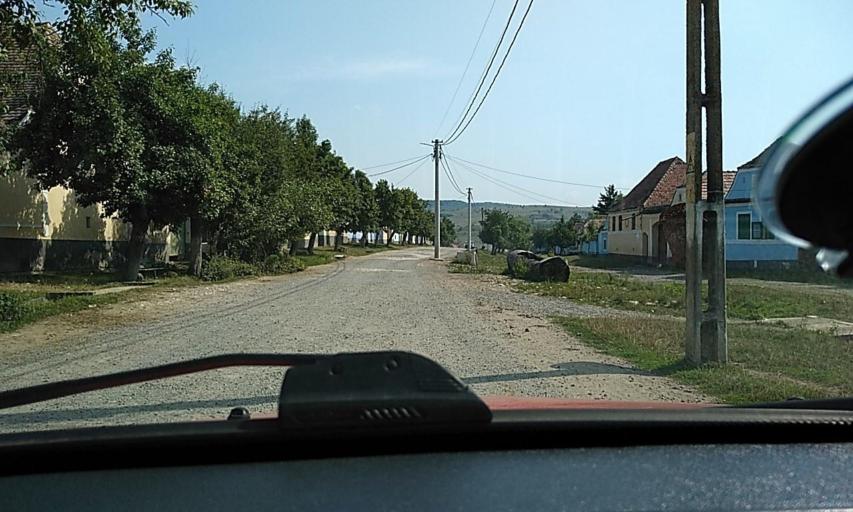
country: RO
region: Brasov
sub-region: Oras Rupea
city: Fiser
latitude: 46.0555
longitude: 25.0944
